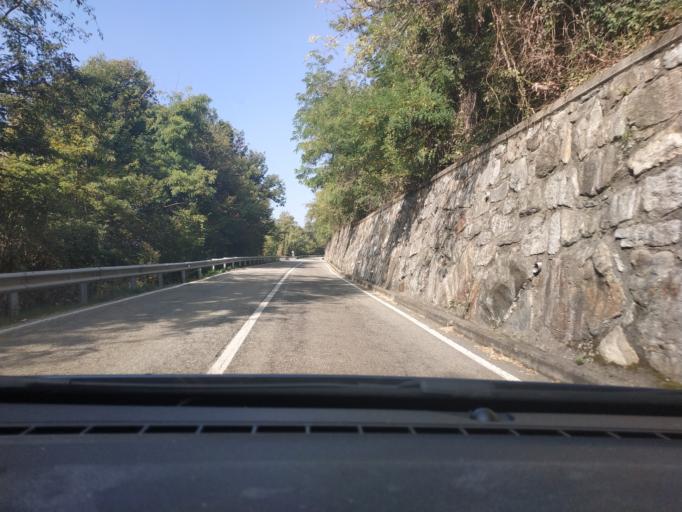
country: IT
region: Piedmont
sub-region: Provincia di Torino
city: Chiaverano
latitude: 45.5110
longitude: 7.9044
